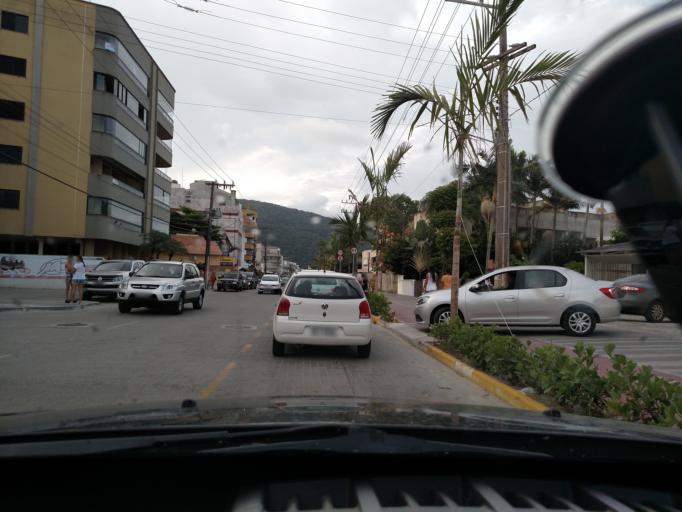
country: BR
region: Santa Catarina
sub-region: Porto Belo
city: Porto Belo
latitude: -27.1407
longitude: -48.5087
